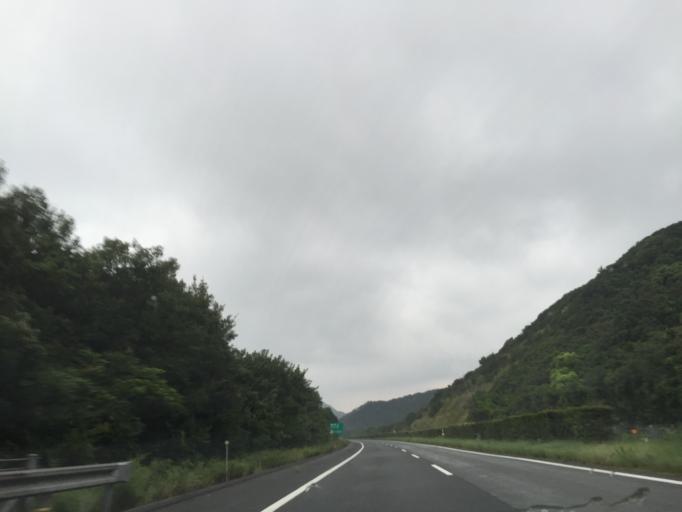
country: JP
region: Tokushima
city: Narutocho-mitsuishi
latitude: 34.2283
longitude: 134.6310
